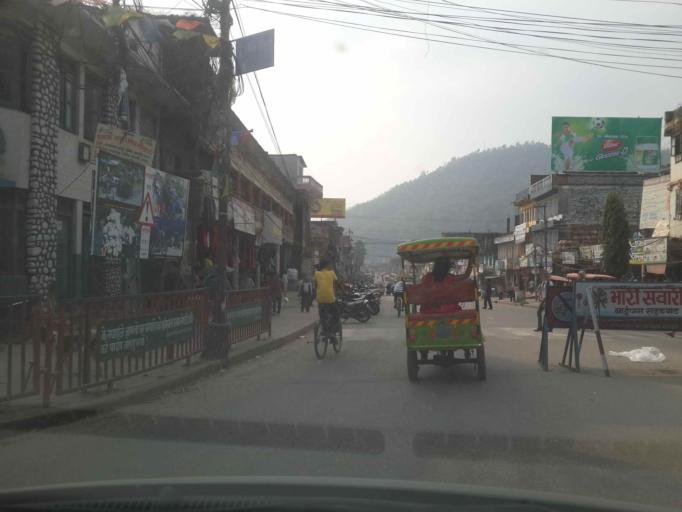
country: NP
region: Central Region
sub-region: Narayani Zone
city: Hitura
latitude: 27.4310
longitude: 85.0319
